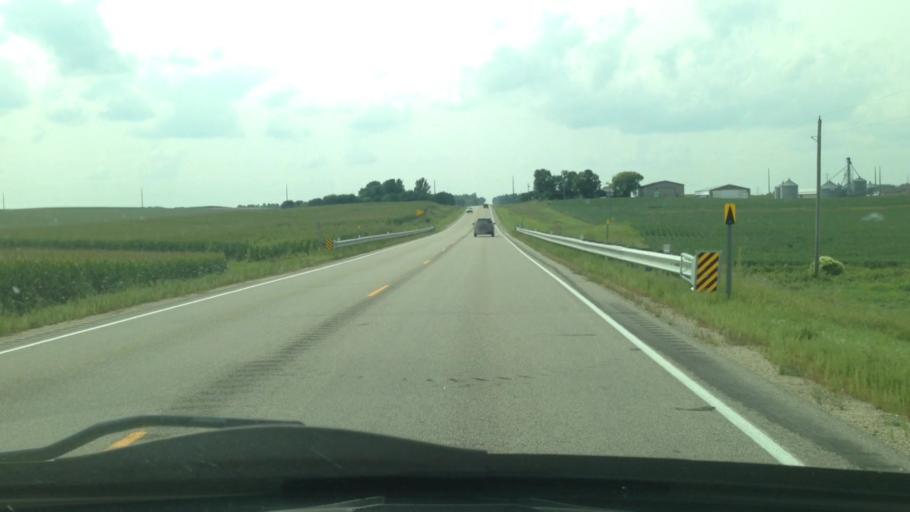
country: US
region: Minnesota
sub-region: Wabasha County
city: Elgin
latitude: 44.1658
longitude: -92.3639
